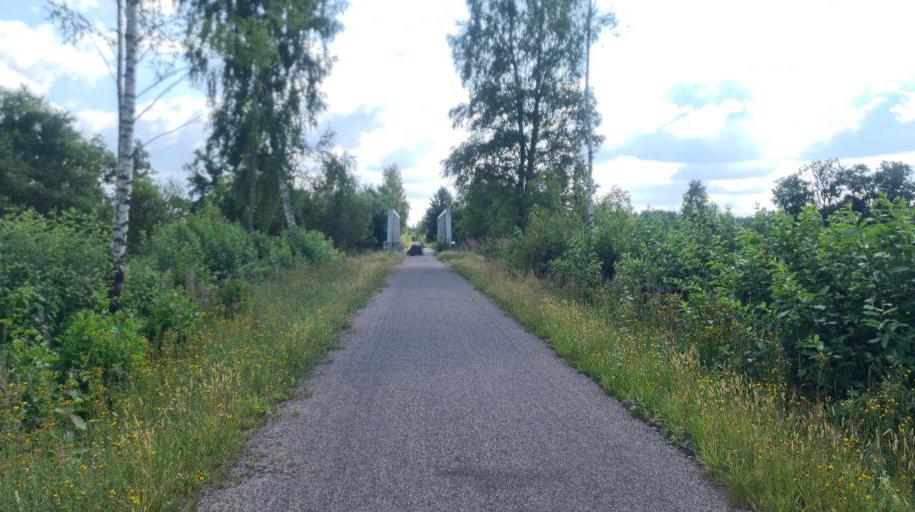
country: SE
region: Kronoberg
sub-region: Ljungby Kommun
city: Ljungby
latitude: 56.7940
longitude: 13.9079
